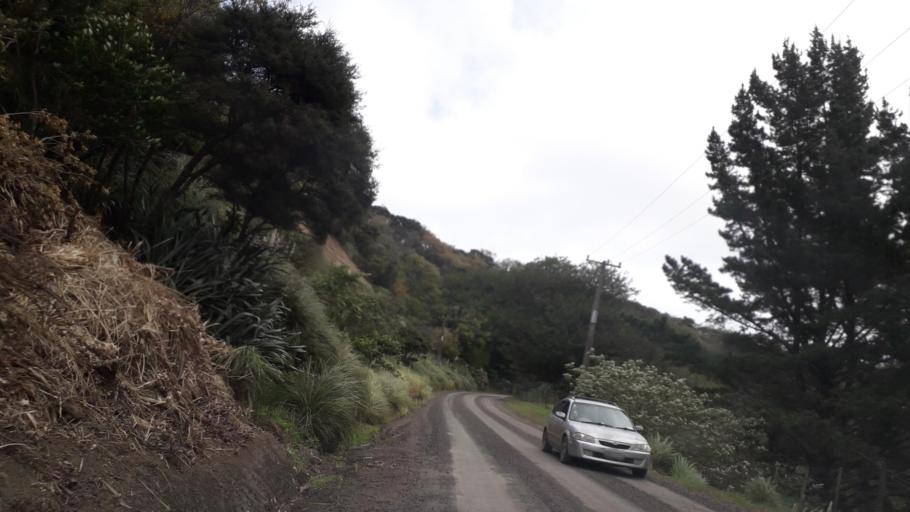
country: NZ
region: Northland
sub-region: Far North District
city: Ahipara
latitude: -35.4407
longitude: 173.3138
